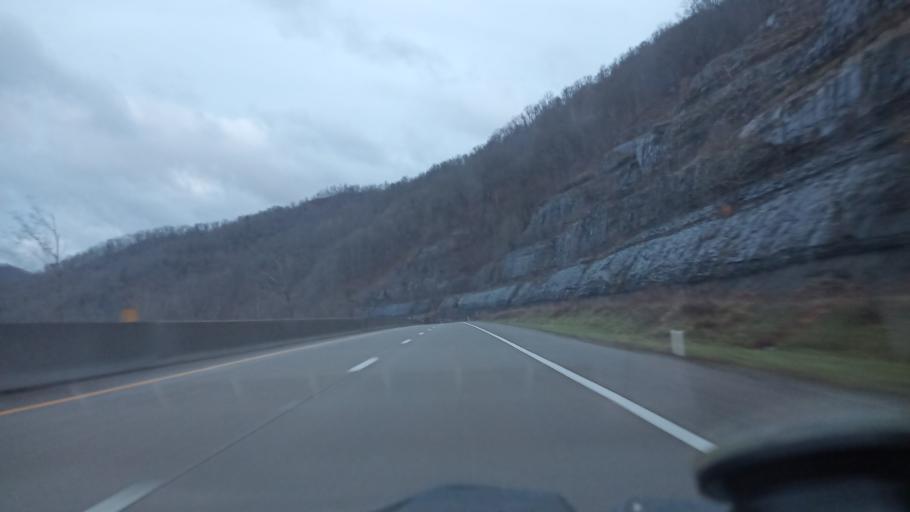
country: US
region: West Virginia
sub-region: Logan County
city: Mallory
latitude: 37.7642
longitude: -81.9178
